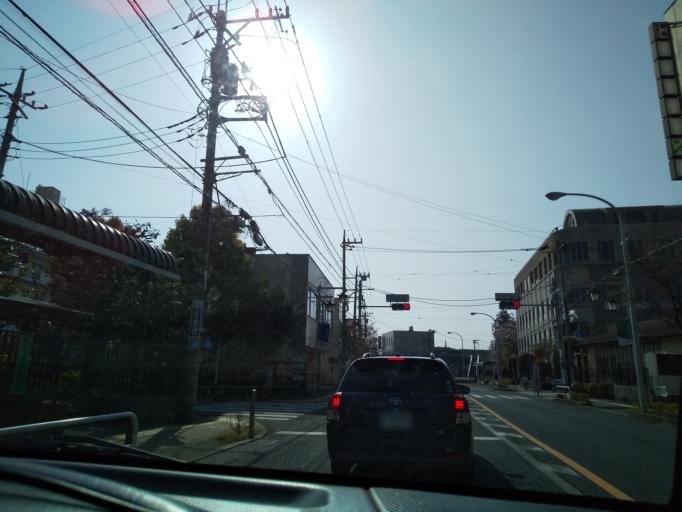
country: JP
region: Tokyo
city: Fussa
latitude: 35.7116
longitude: 139.3635
